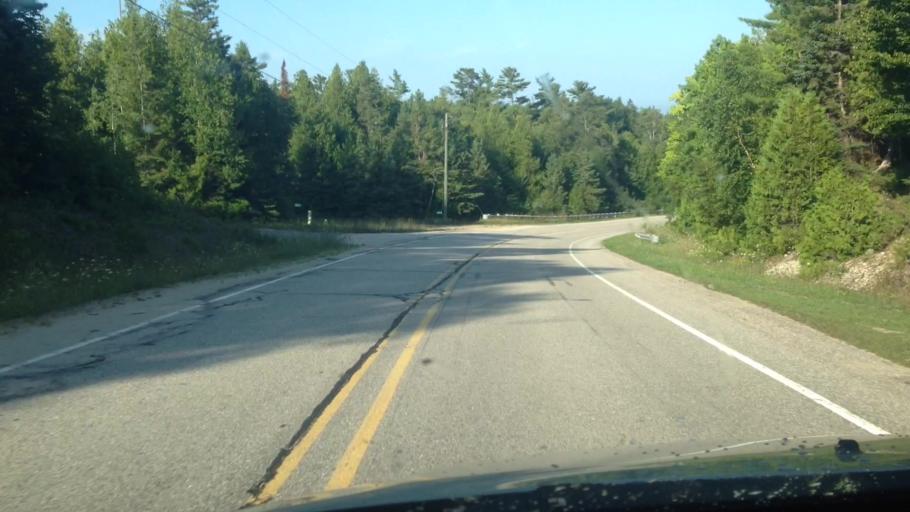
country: US
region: Michigan
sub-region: Mackinac County
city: Saint Ignace
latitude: 45.8926
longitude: -84.8262
